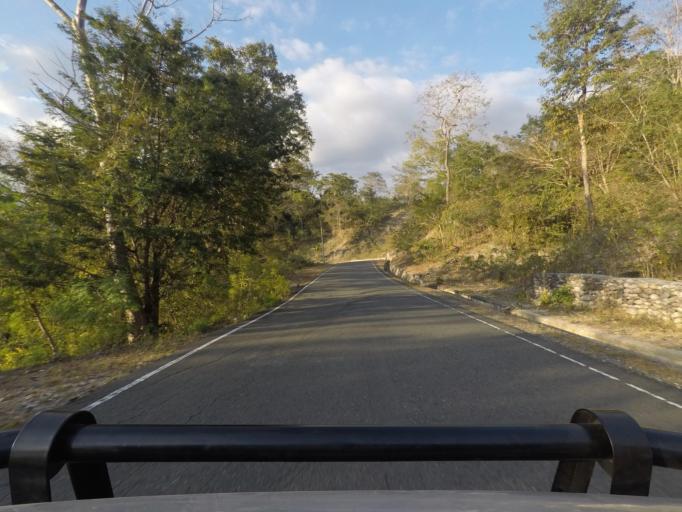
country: TL
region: Bobonaro
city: Maliana
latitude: -8.9529
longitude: 125.0918
